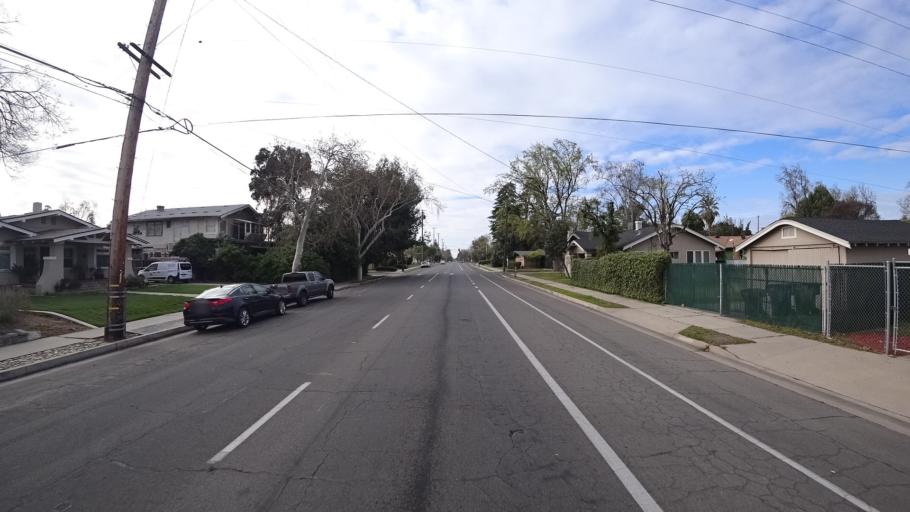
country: US
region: California
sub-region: Fresno County
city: Fresno
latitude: 36.7737
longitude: -119.8011
